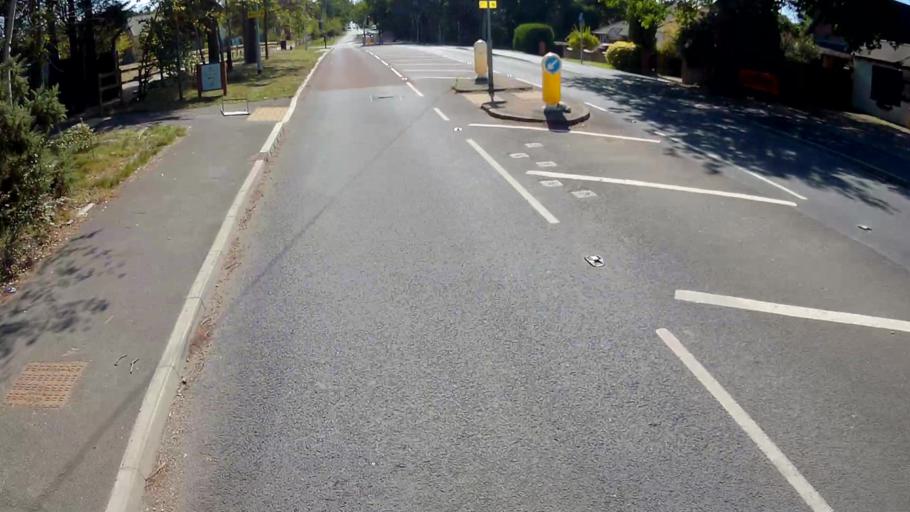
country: GB
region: England
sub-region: Bracknell Forest
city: Crowthorne
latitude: 51.3792
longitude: -0.7910
